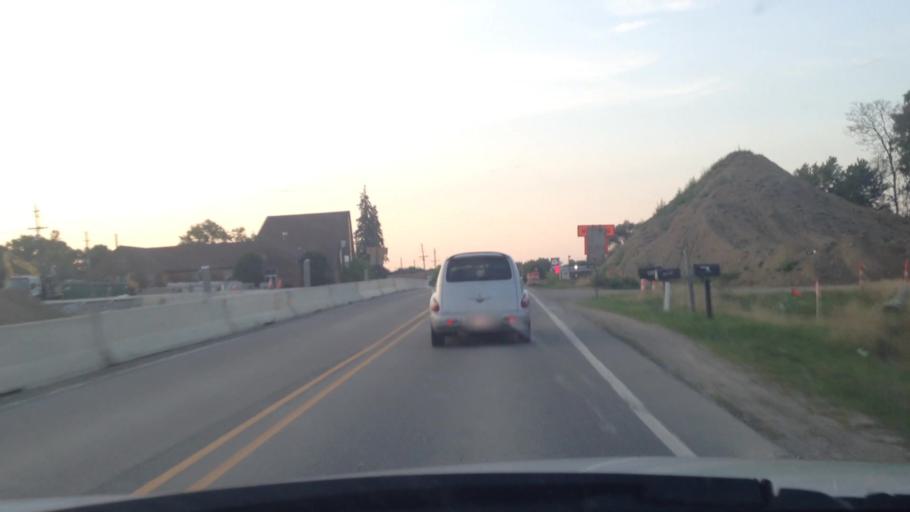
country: US
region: Michigan
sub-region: Oakland County
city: Auburn Hills
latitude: 42.7212
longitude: -83.3074
